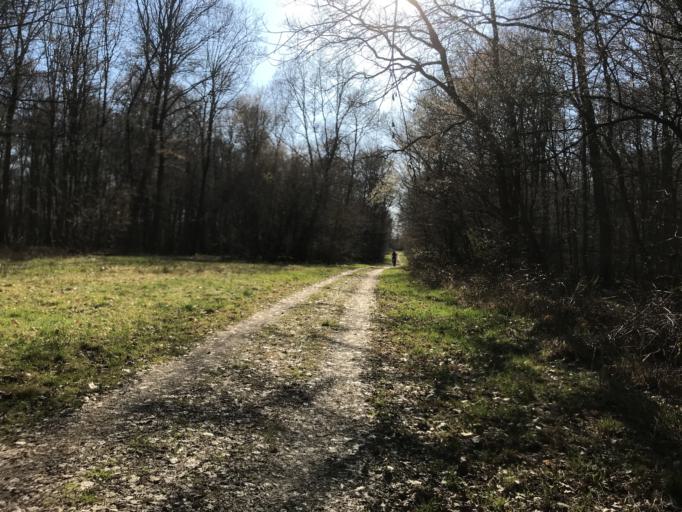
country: DE
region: Rheinland-Pfalz
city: Essenheim
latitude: 49.9561
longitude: 8.1638
